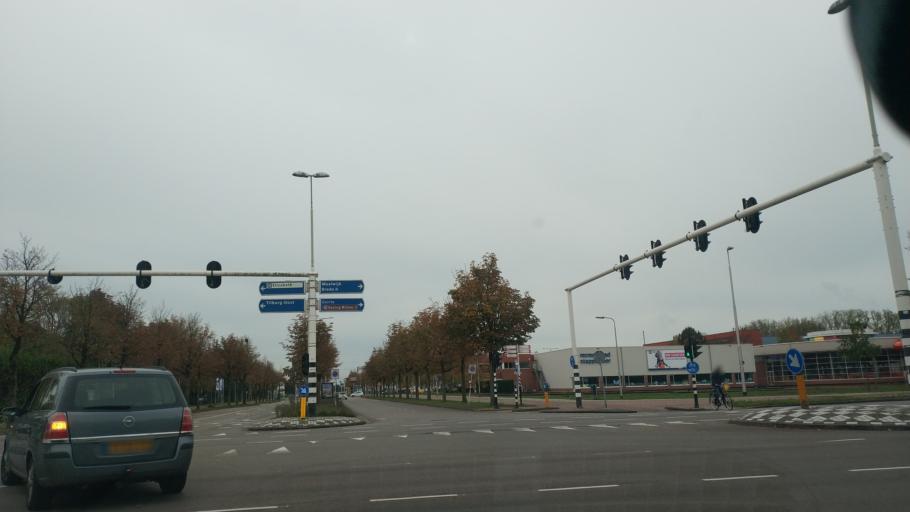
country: NL
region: North Brabant
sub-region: Gemeente Tilburg
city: Tilburg
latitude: 51.5441
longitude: 5.0773
